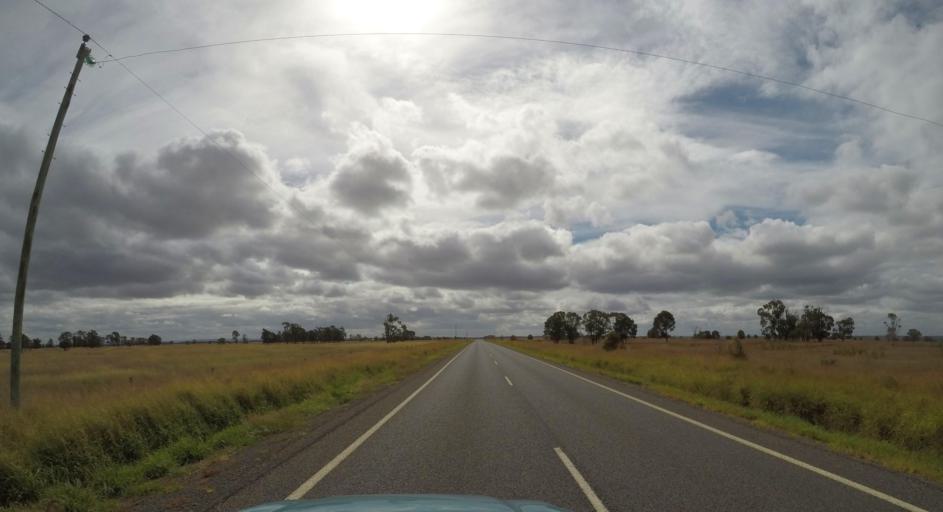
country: AU
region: Queensland
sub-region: South Burnett
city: Kingaroy
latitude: -26.3389
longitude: 151.2526
